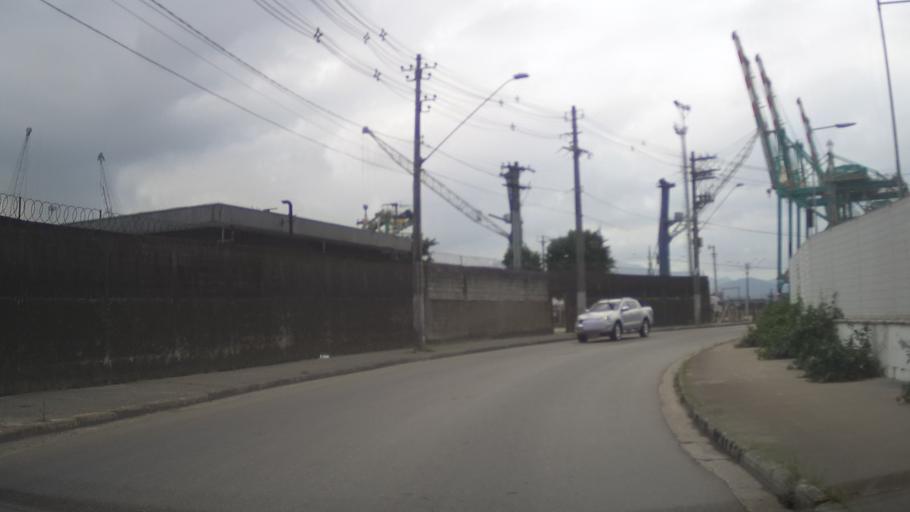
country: BR
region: Sao Paulo
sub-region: Santos
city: Santos
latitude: -23.9300
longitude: -46.3365
